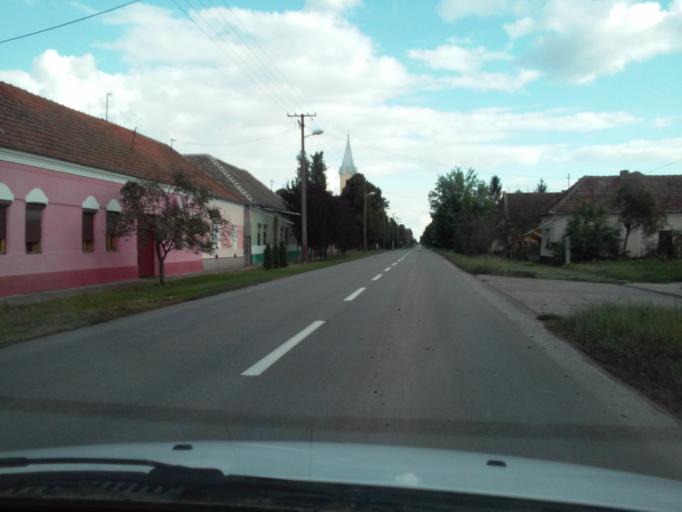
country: RS
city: Sajan
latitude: 45.8441
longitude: 20.2728
